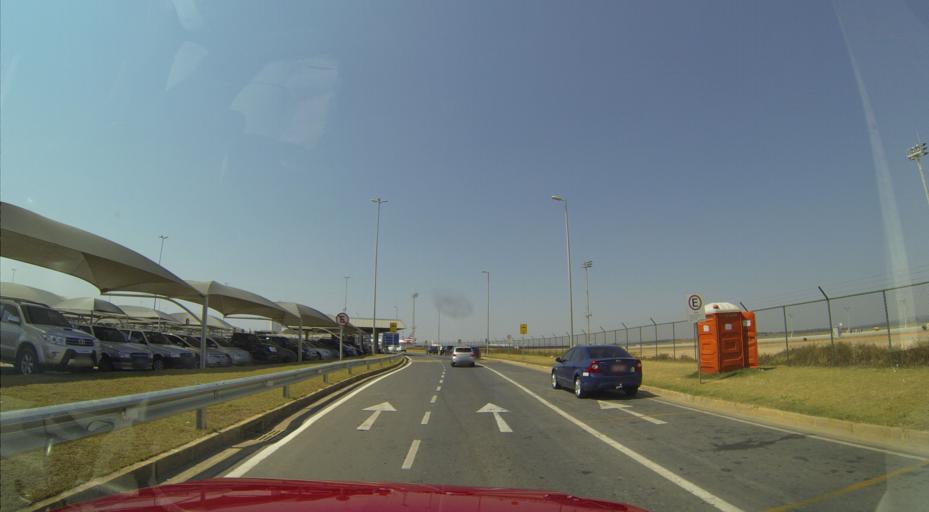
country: BR
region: Minas Gerais
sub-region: Lagoa Santa
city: Lagoa Santa
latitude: -19.6287
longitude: -43.9668
